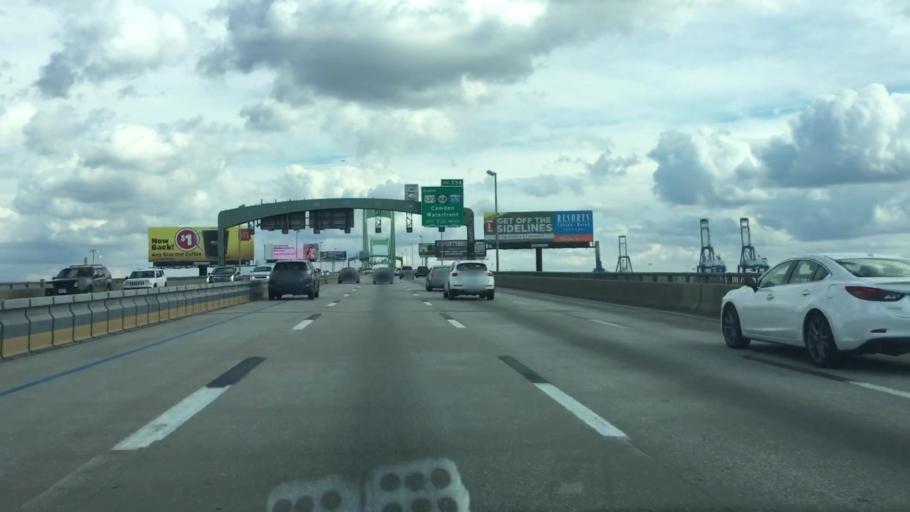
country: US
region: New Jersey
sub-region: Camden County
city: Camden
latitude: 39.9077
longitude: -75.1441
